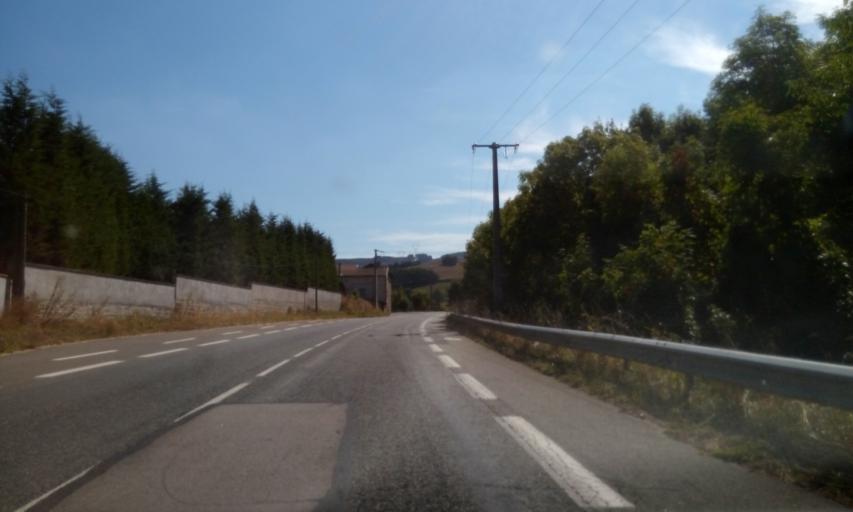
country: FR
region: Rhone-Alpes
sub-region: Departement du Rhone
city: Amplepuis
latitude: 45.9726
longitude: 4.3479
